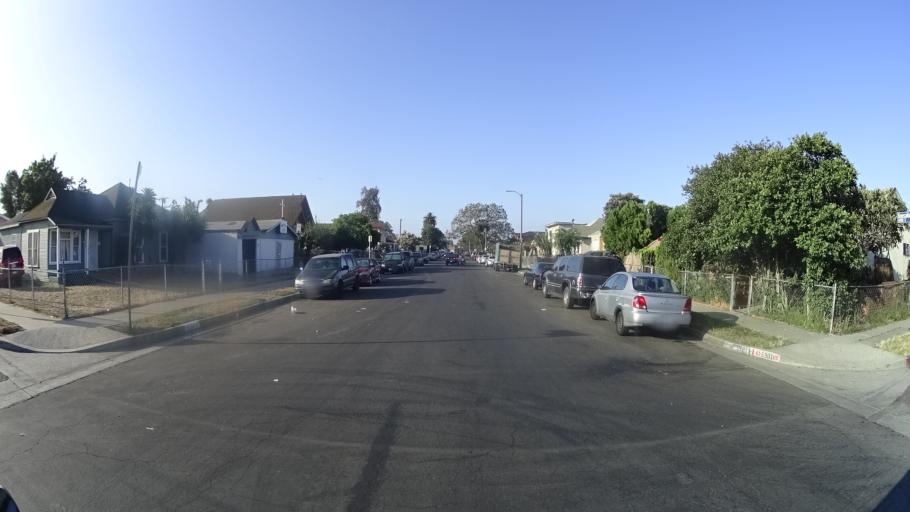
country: US
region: California
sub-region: Los Angeles County
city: Westmont
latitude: 33.9773
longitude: -118.2860
